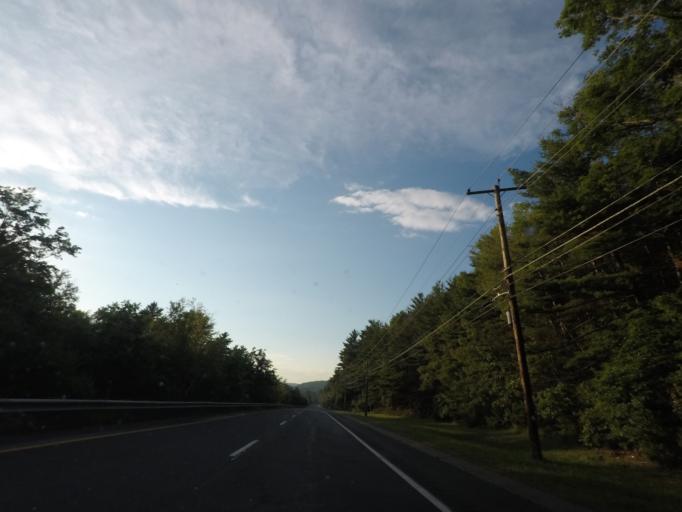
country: US
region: Massachusetts
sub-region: Hampden County
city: Brimfield
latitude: 42.1227
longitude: -72.2505
